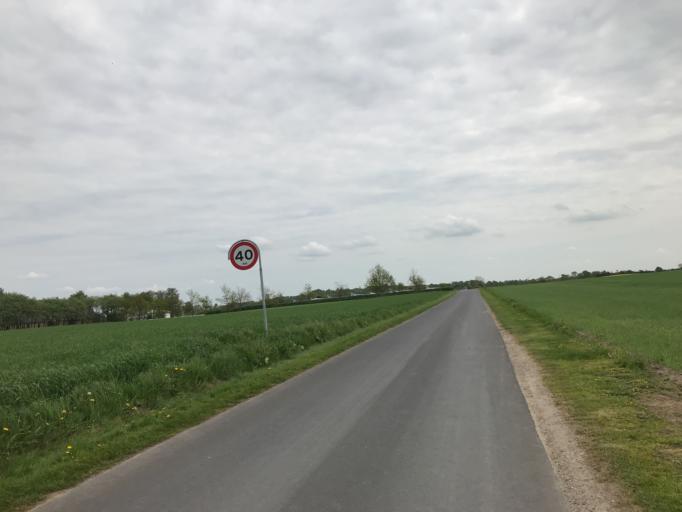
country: DK
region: South Denmark
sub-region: Assens Kommune
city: Assens
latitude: 55.3340
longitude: 9.8849
